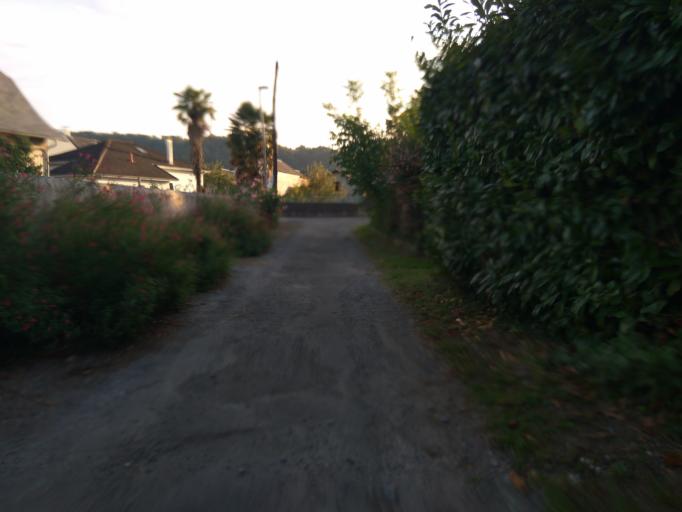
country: FR
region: Aquitaine
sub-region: Departement des Pyrenees-Atlantiques
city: Bizanos
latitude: 43.2787
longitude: -0.3528
